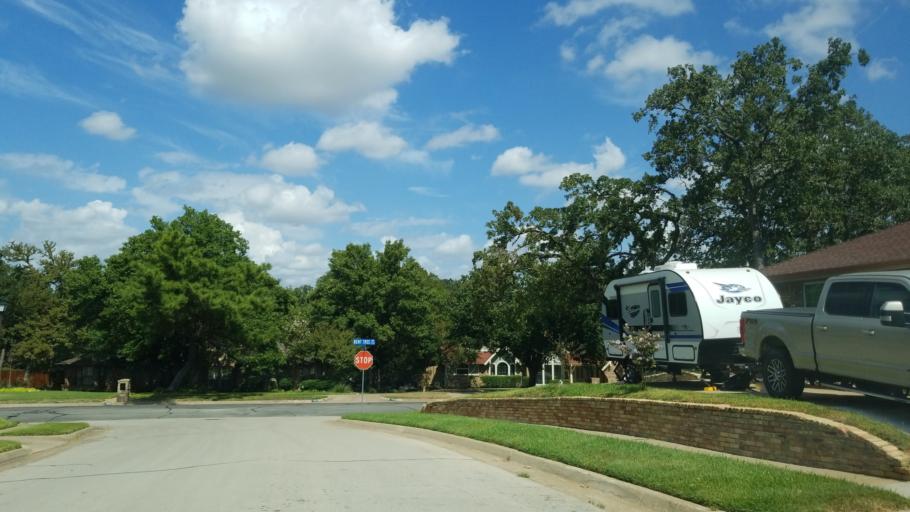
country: US
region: Texas
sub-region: Tarrant County
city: Euless
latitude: 32.8642
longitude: -97.0927
